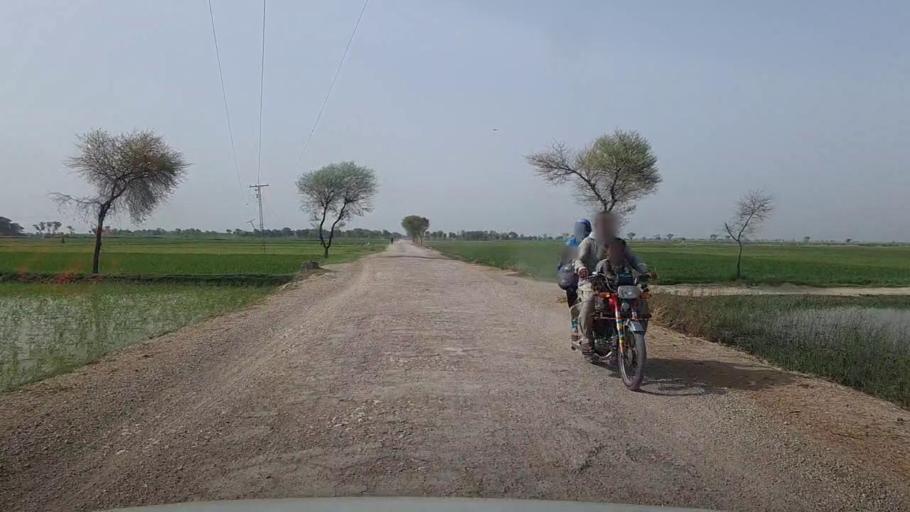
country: PK
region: Sindh
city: Mehar
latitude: 27.1106
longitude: 67.8200
